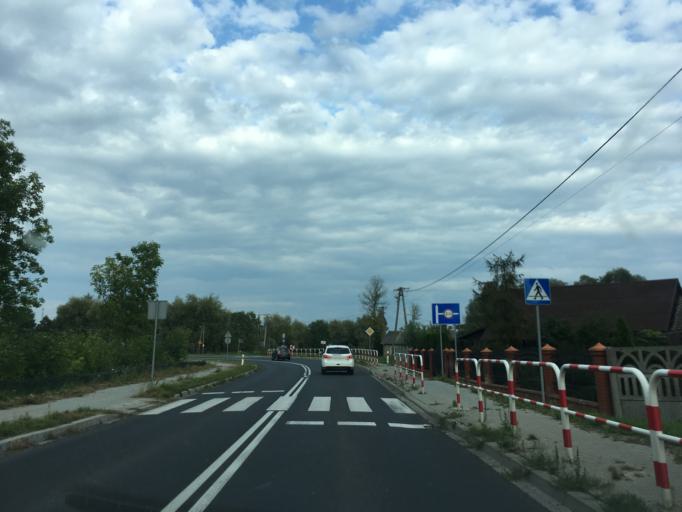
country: PL
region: Swietokrzyskie
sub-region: Powiat wloszczowski
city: Wloszczowa
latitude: 50.8068
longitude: 19.9249
